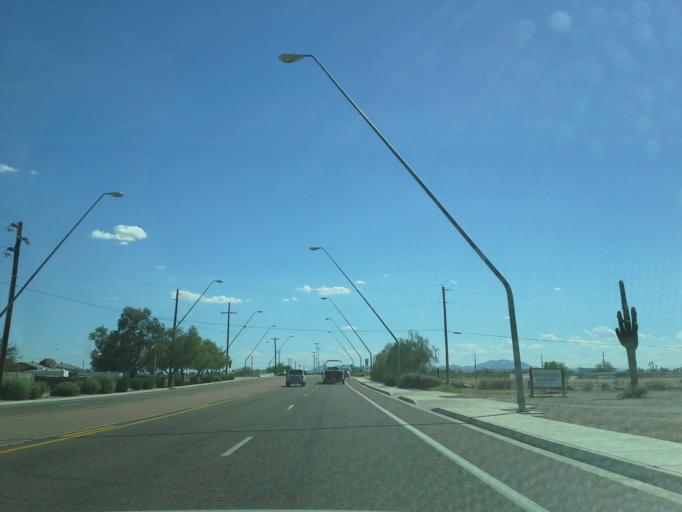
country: US
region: Arizona
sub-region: Pinal County
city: Apache Junction
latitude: 33.4276
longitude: -111.6327
